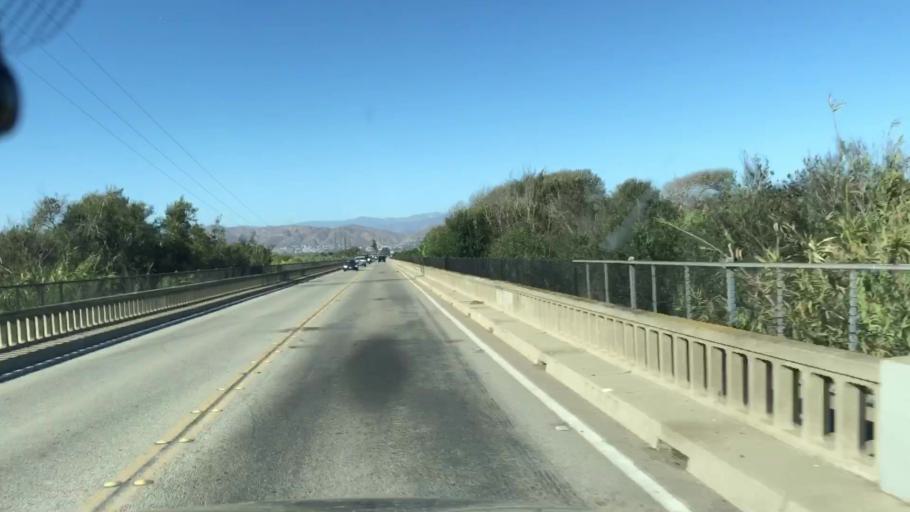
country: US
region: California
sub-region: Ventura County
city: Oxnard Shores
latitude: 34.2317
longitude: -119.2562
